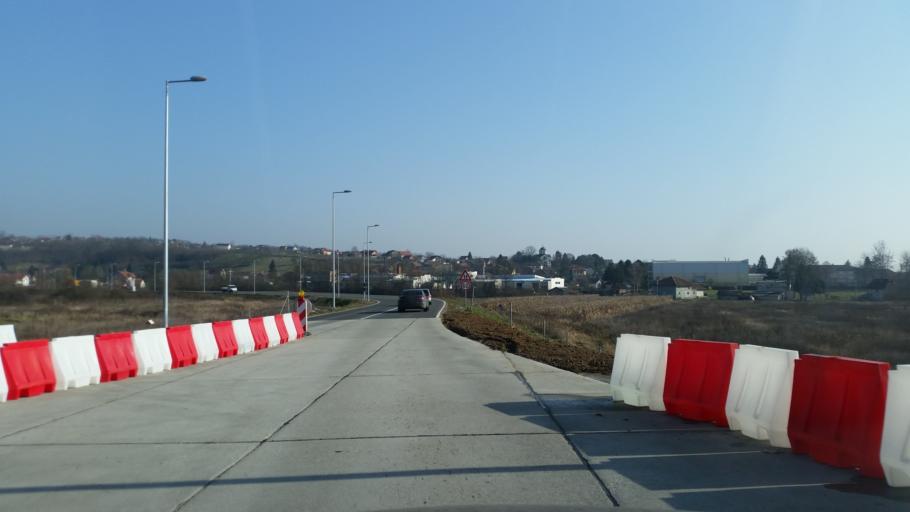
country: RS
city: Prislonica
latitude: 43.9172
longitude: 20.4010
